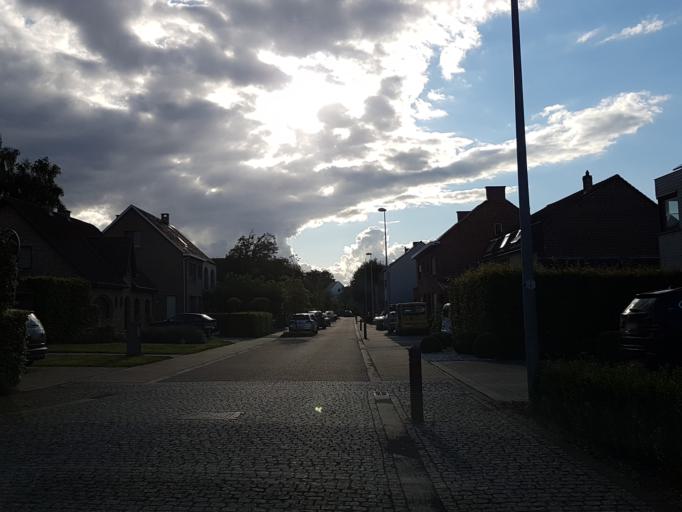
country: BE
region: Flanders
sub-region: Provincie Vlaams-Brabant
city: Herent
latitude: 50.9072
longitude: 4.6277
